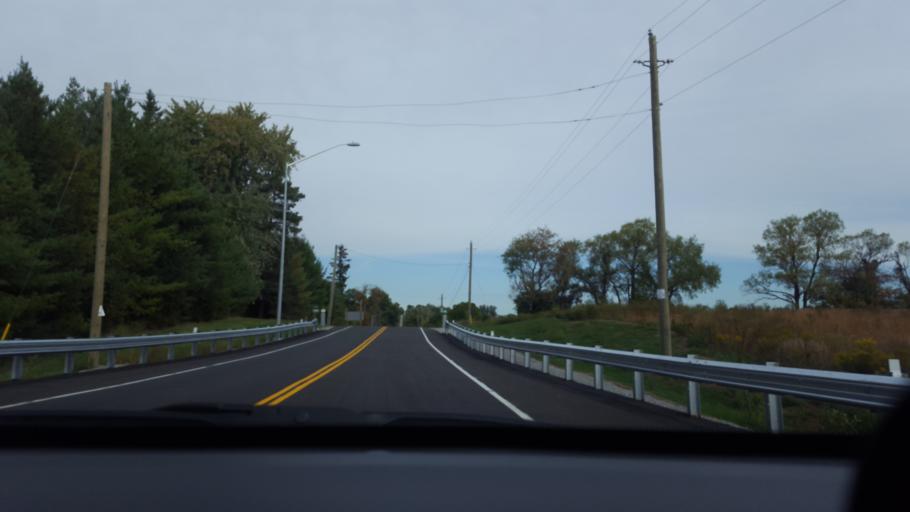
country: CA
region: Ontario
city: Newmarket
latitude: 44.0021
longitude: -79.5477
